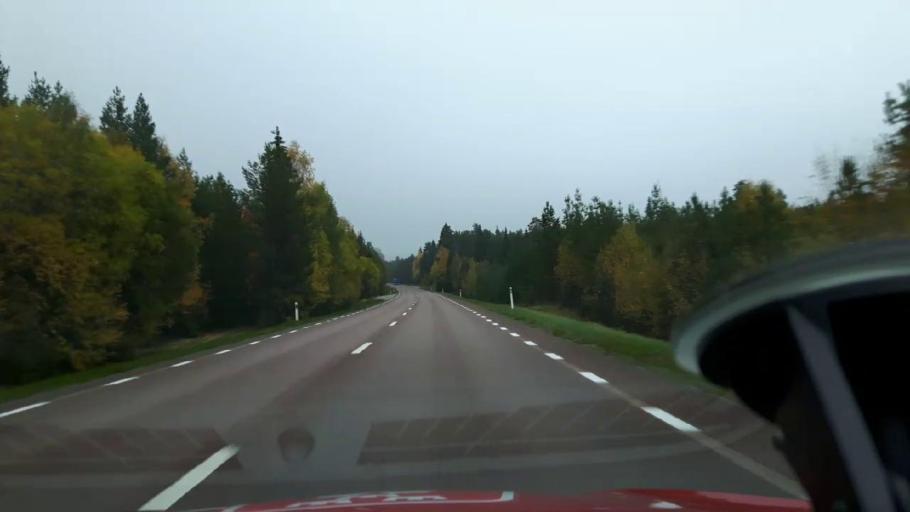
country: SE
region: Jaemtland
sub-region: Bergs Kommun
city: Hoverberg
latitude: 62.6101
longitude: 14.4001
